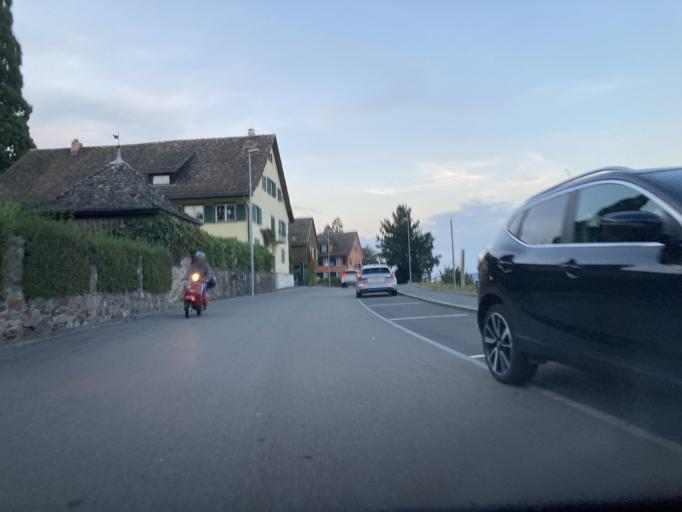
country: CH
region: Zurich
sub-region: Bezirk Horgen
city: Kilchberg / Kilchberg (Dorfkern)
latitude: 47.3181
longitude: 8.5463
